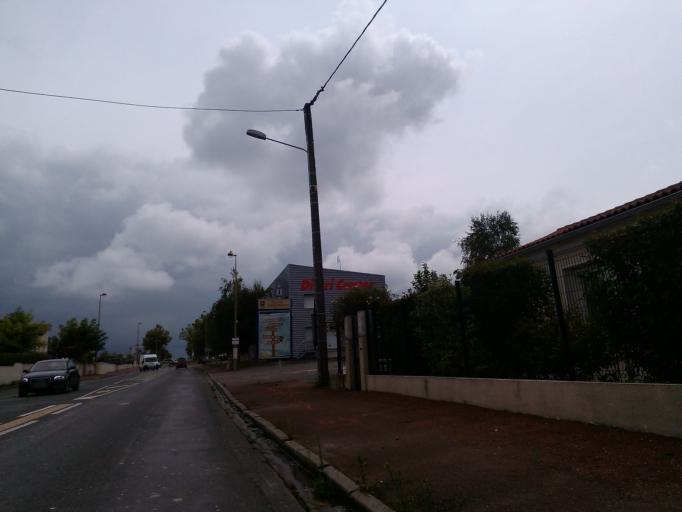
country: FR
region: Poitou-Charentes
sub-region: Departement de la Charente
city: Saint-Brice
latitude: 45.6861
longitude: -0.3069
